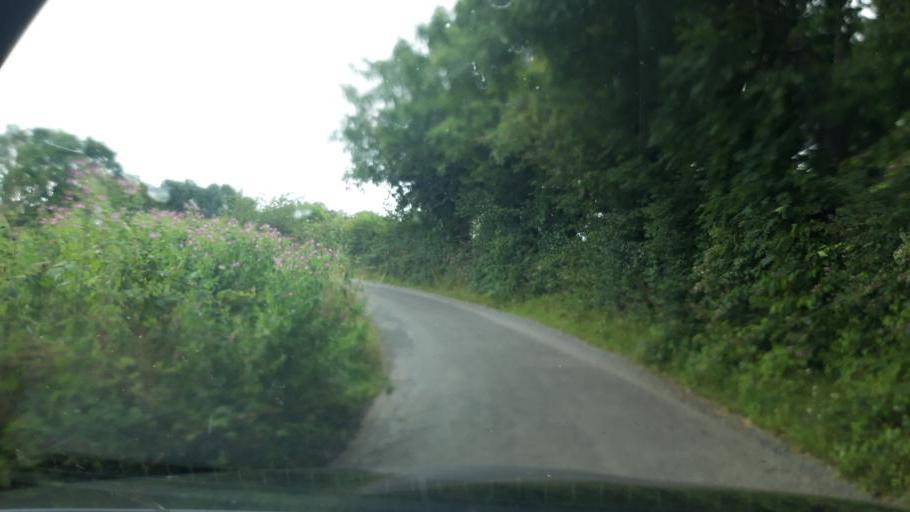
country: IE
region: Leinster
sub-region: Kilkenny
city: Graiguenamanagh
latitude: 52.6009
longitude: -7.0360
